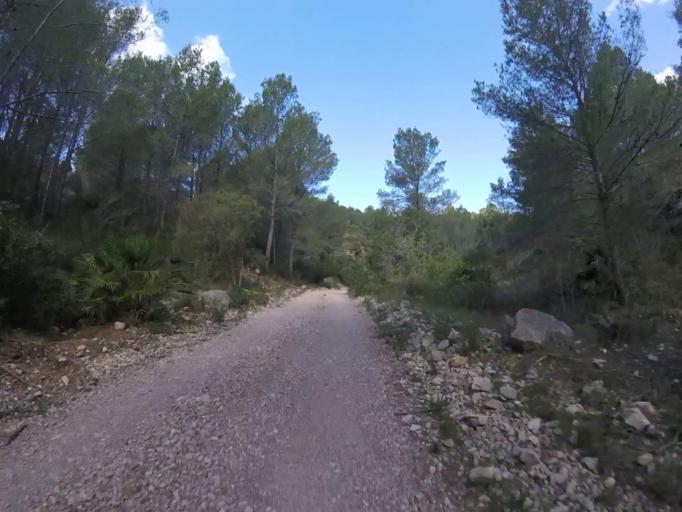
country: ES
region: Valencia
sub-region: Provincia de Castello
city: Alcoceber
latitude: 40.2958
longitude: 0.3143
